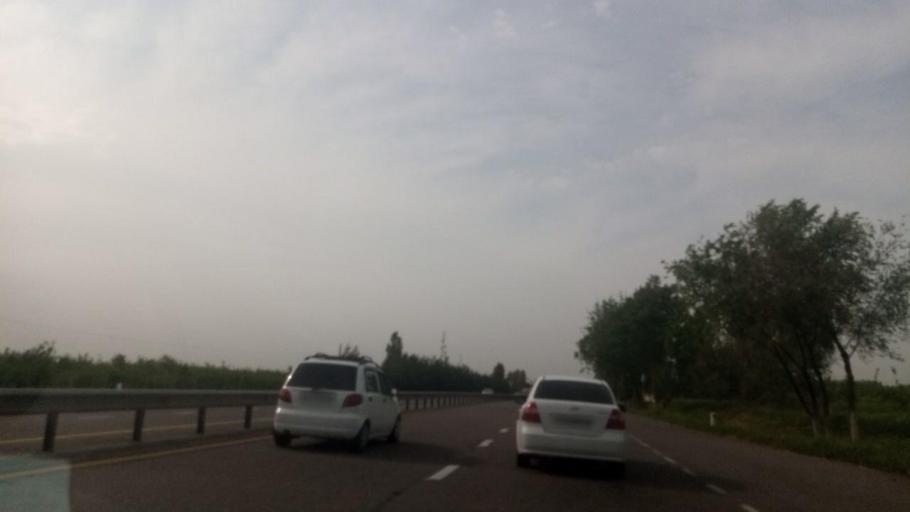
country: UZ
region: Toshkent
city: Tuytepa
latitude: 41.1149
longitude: 69.4459
